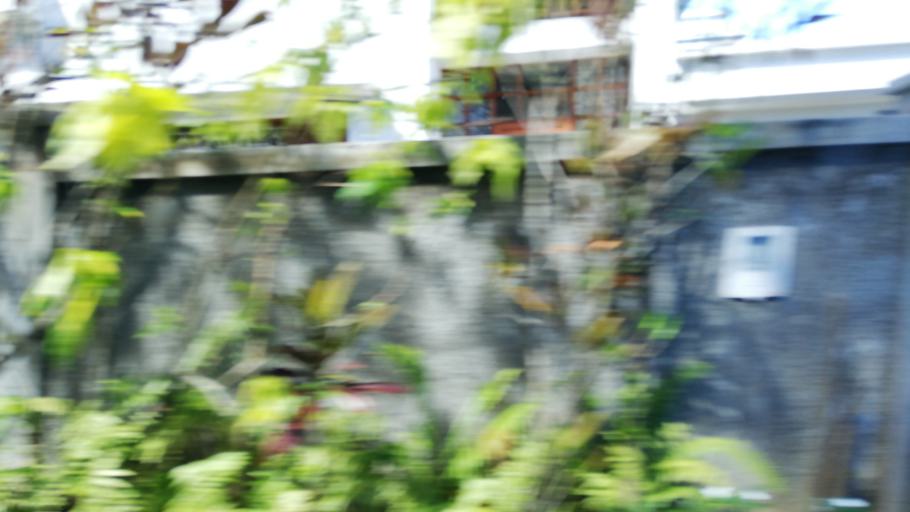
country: MU
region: Plaines Wilhems
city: Ebene
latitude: -20.2318
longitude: 57.4739
